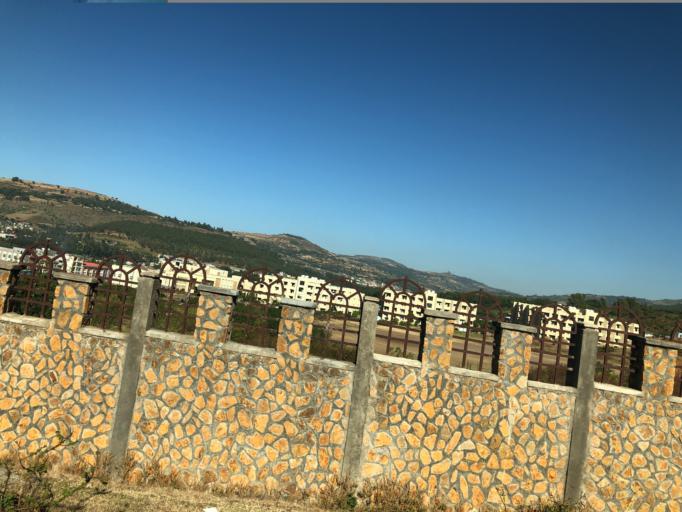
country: ET
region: Amhara
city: Gondar
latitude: 12.5747
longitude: 37.4462
